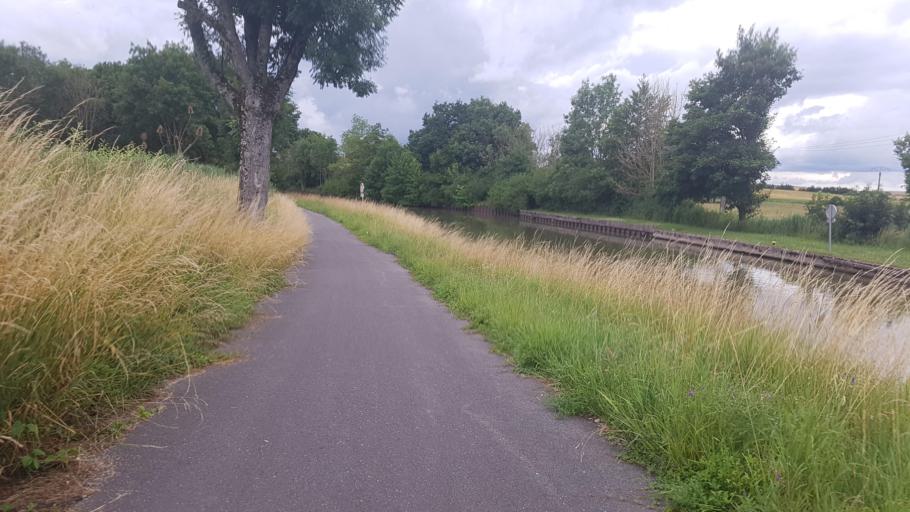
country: FR
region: Lorraine
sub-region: Departement de la Moselle
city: Dieuze
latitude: 48.6884
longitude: 6.6633
